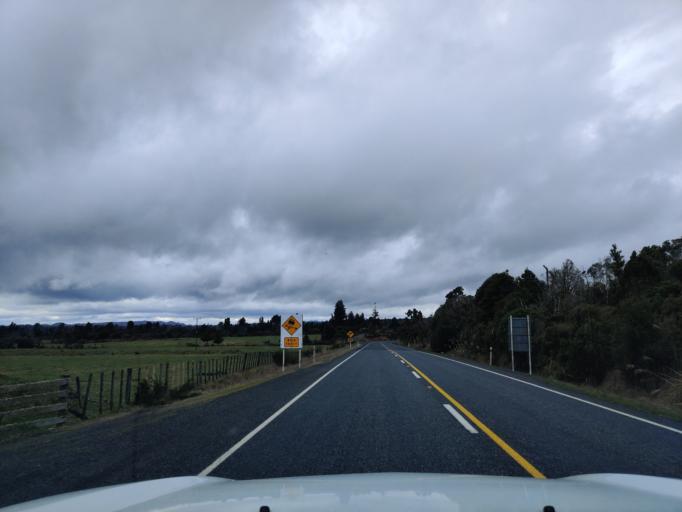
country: NZ
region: Manawatu-Wanganui
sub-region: Ruapehu District
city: Waiouru
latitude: -39.2823
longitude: 175.3863
